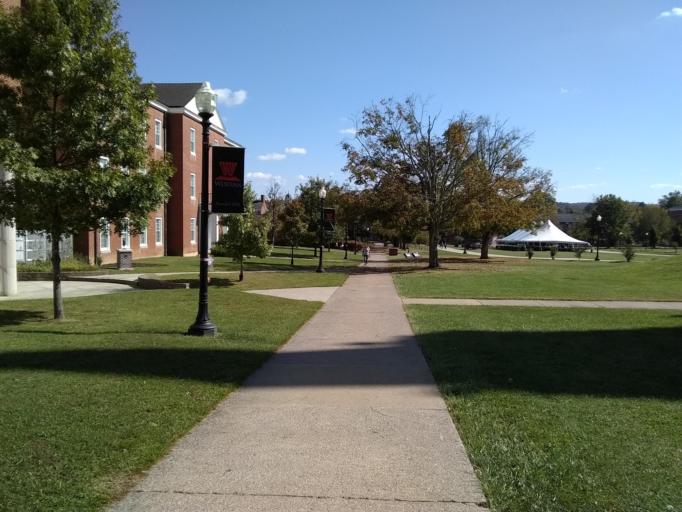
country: US
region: West Virginia
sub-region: Upshur County
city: Buckhannon
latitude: 38.9900
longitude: -80.2187
